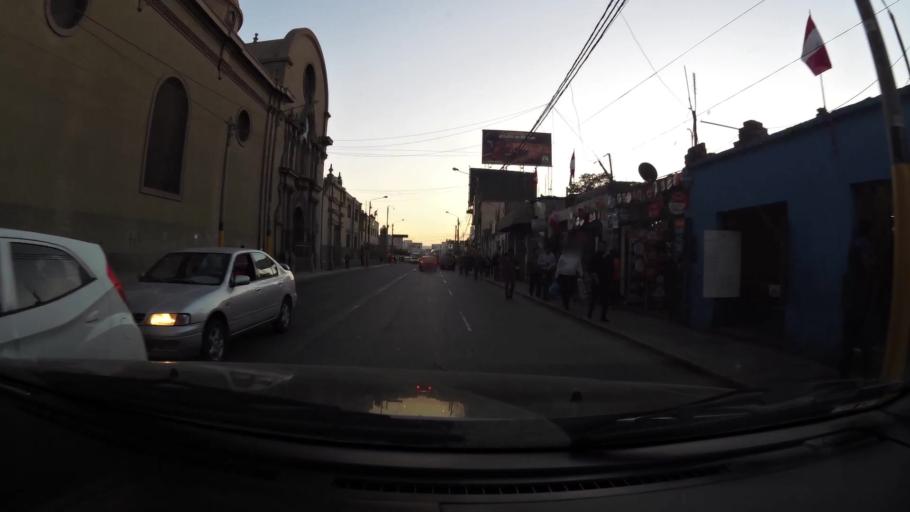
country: PE
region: Ica
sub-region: Provincia de Ica
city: Ica
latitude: -14.0641
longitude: -75.7313
